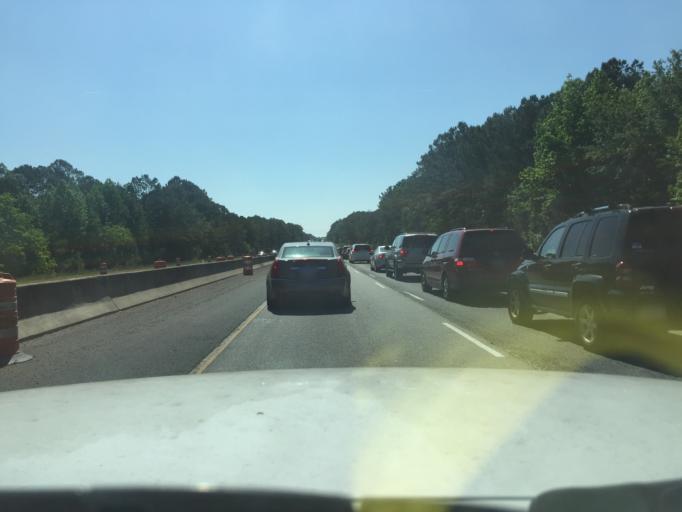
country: US
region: Georgia
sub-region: Chatham County
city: Georgetown
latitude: 31.9966
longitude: -81.2401
